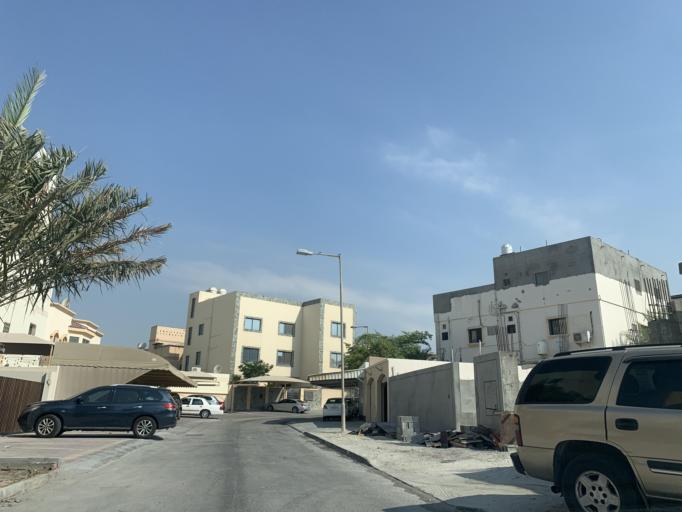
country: BH
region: Central Governorate
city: Madinat Hamad
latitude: 26.1021
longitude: 50.4996
